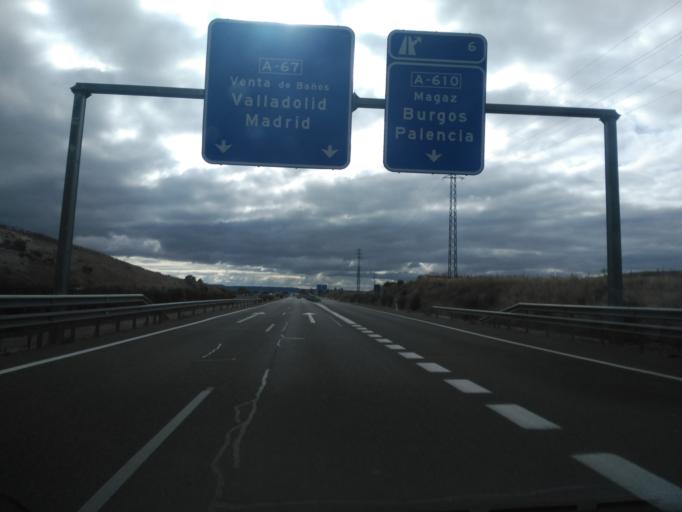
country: ES
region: Castille and Leon
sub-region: Provincia de Palencia
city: Palencia
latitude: 41.9883
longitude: -4.5027
